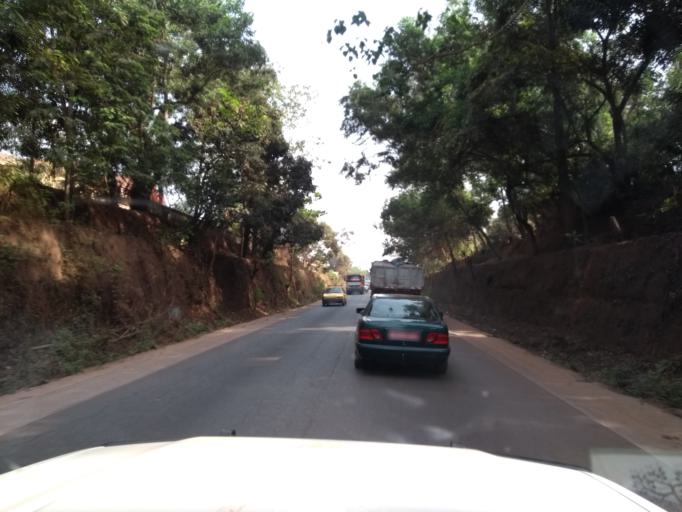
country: GN
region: Kindia
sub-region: Prefecture de Dubreka
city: Dubreka
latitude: 9.8176
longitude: -13.4824
